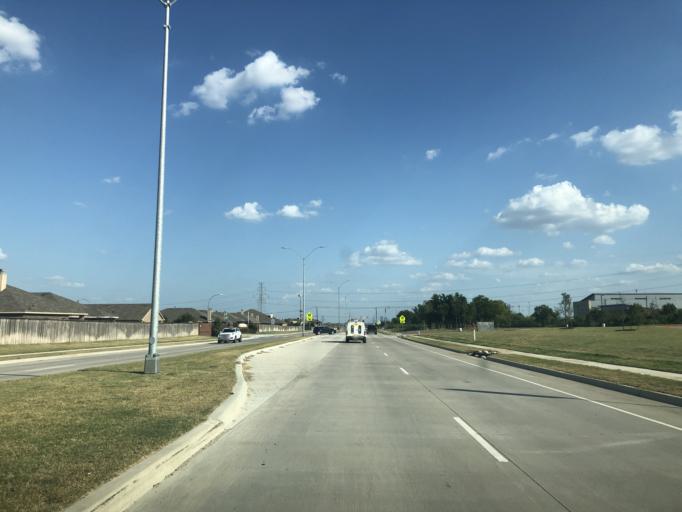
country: US
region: Texas
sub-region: Tarrant County
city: Saginaw
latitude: 32.8428
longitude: -97.3887
